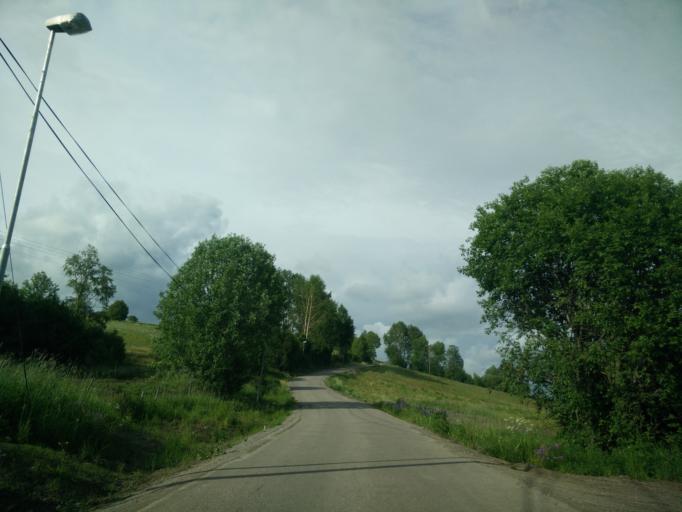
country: SE
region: Vaesternorrland
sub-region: Sundsvalls Kommun
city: Sundsvall
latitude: 62.4205
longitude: 17.2444
